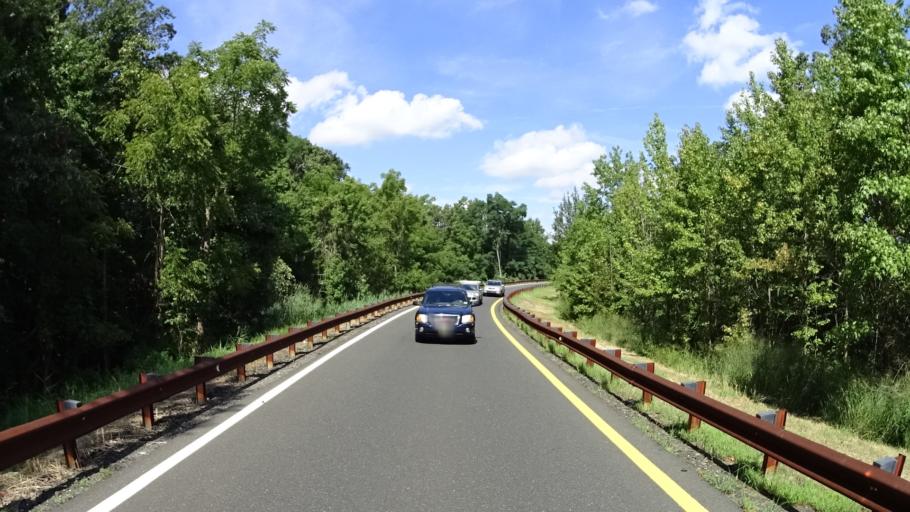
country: US
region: New Jersey
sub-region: Monmouth County
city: Strathmore
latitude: 40.4037
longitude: -74.1963
